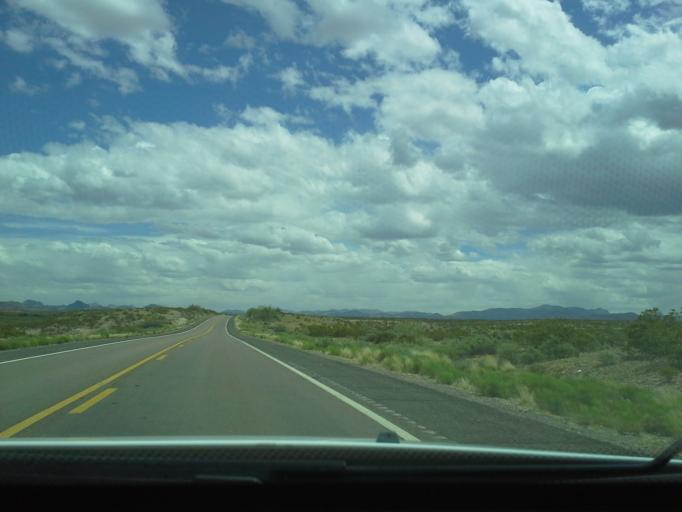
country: US
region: Arizona
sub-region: Graham County
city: Safford
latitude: 32.8014
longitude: -109.5715
